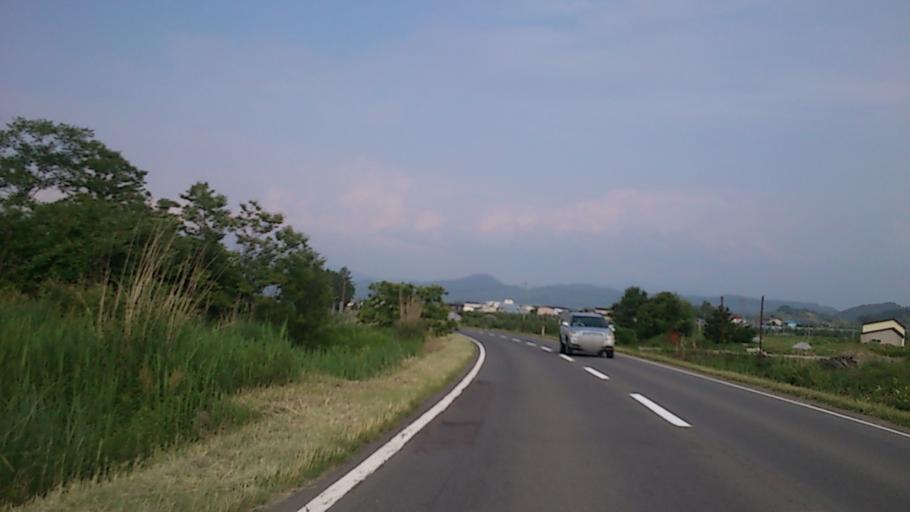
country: JP
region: Aomori
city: Hirosaki
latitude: 40.5578
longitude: 140.5053
